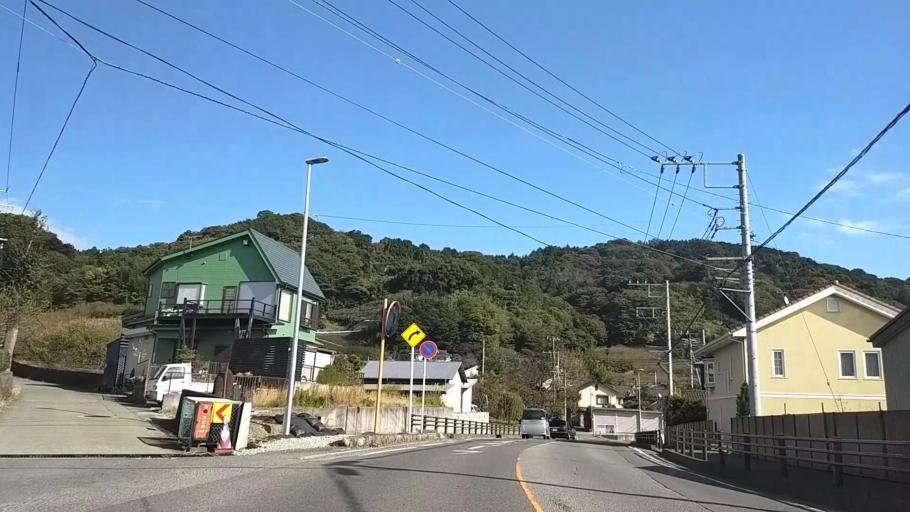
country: JP
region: Kanagawa
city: Odawara
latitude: 35.3017
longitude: 139.1944
